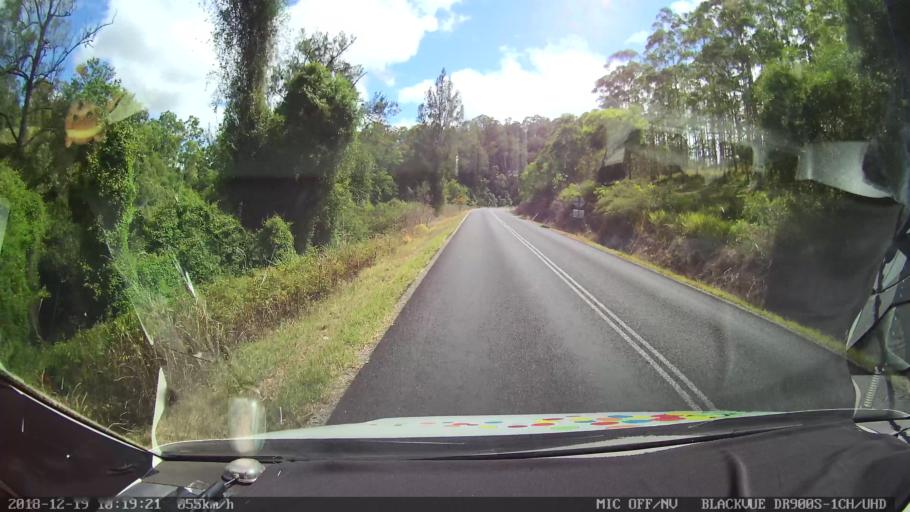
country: AU
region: New South Wales
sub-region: Kyogle
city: Kyogle
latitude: -28.5998
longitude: 153.0461
